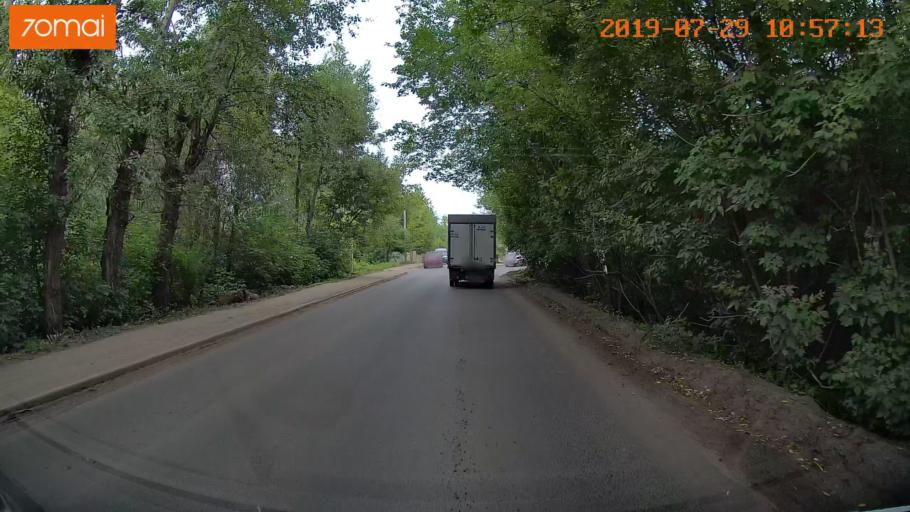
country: RU
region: Ivanovo
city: Bogorodskoye
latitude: 56.9879
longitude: 41.0355
